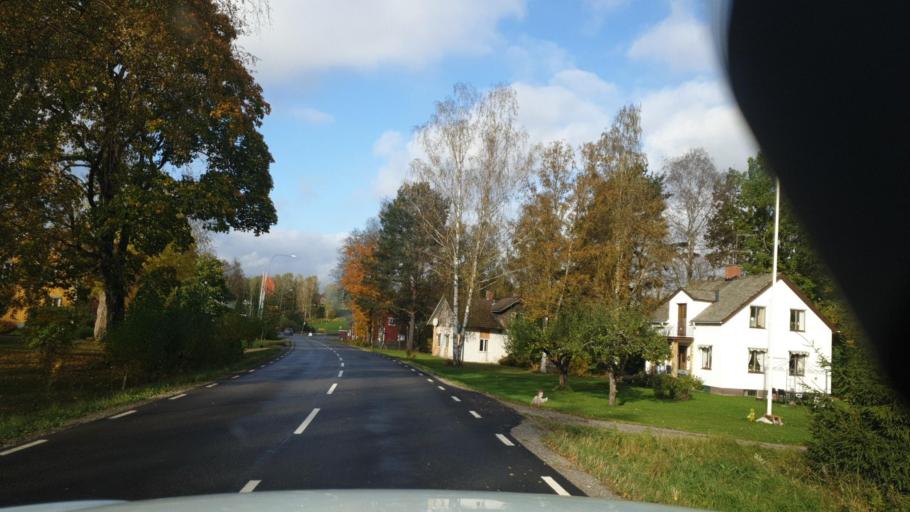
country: SE
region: Vaermland
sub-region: Arvika Kommun
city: Arvika
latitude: 59.5478
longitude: 12.5671
